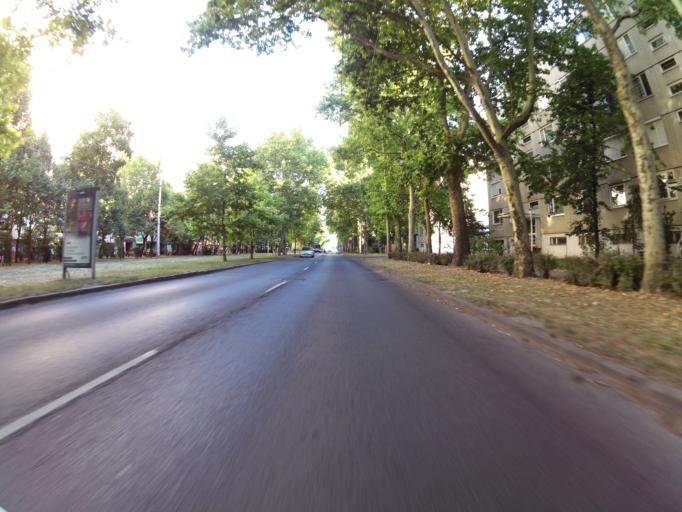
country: HU
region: Csongrad
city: Szeged
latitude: 46.2652
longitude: 20.1682
